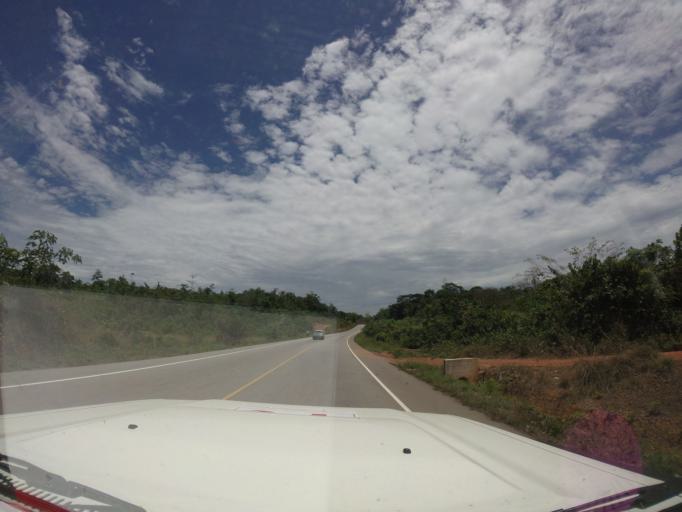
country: LR
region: Bong
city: Gbarnga
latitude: 6.8407
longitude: -9.8417
